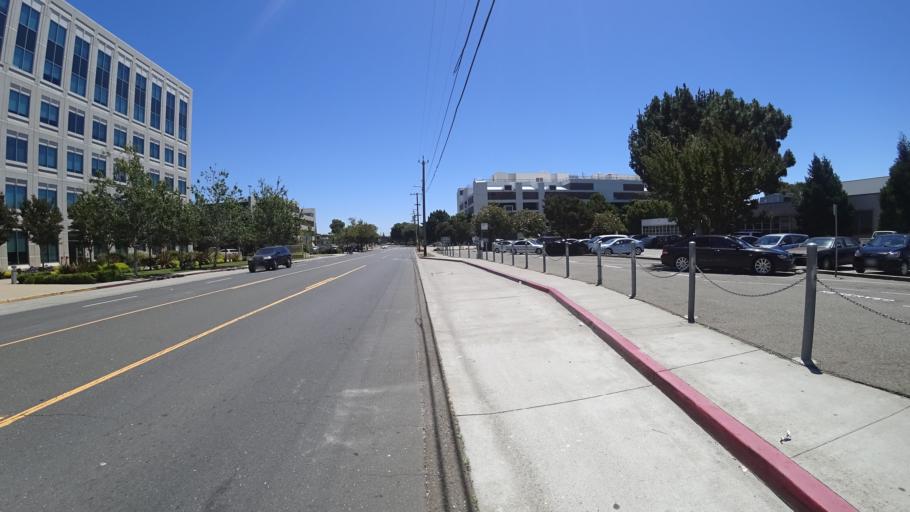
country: US
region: California
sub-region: Alameda County
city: Hayward
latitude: 37.6585
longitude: -122.0945
